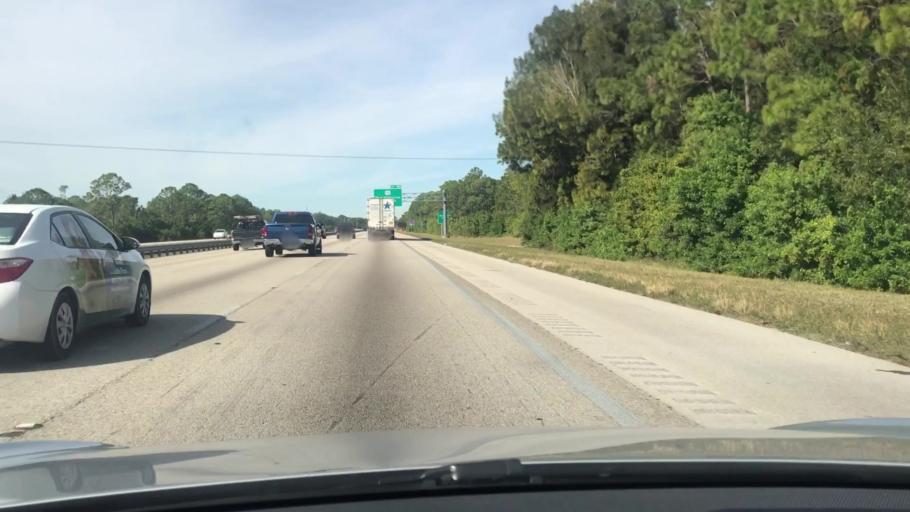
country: US
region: Florida
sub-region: Brevard County
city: June Park
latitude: 28.0647
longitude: -80.6940
